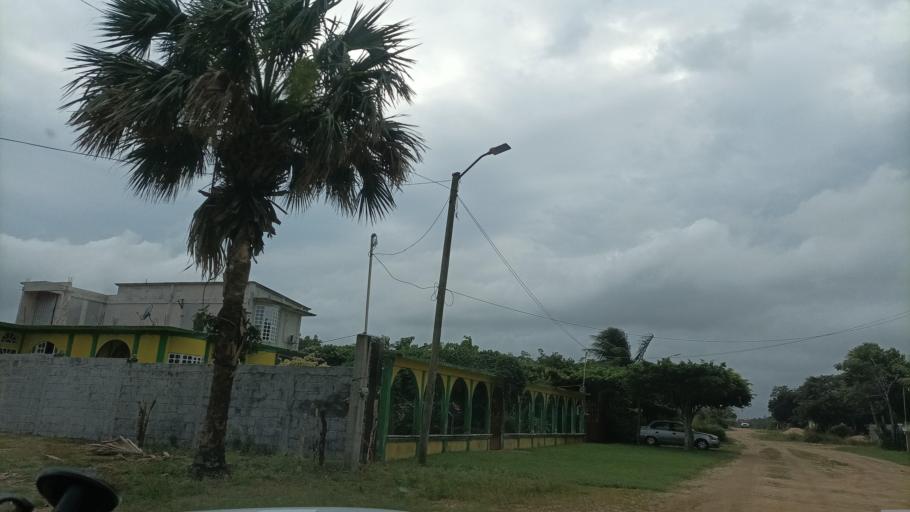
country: MX
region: Veracruz
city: Agua Dulce
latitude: 18.2071
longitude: -94.1433
